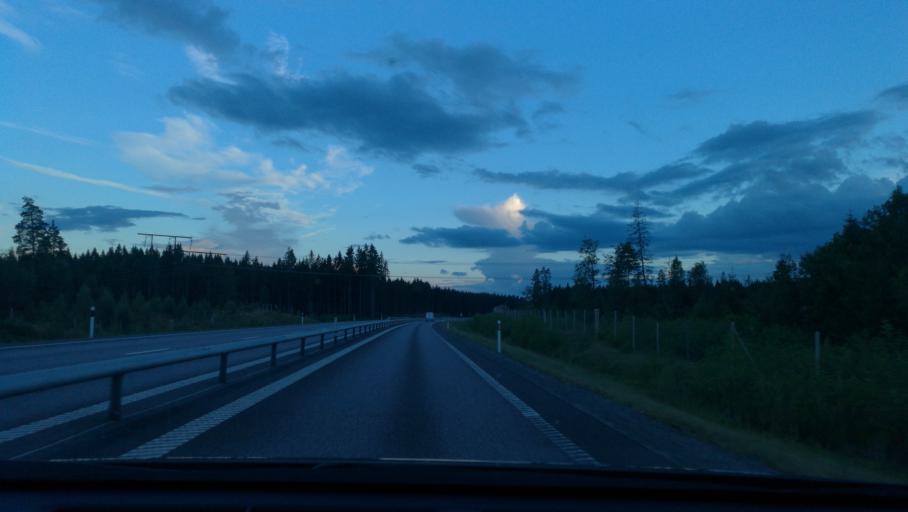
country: SE
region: Soedermanland
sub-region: Katrineholms Kommun
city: Katrineholm
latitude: 58.9480
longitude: 16.2170
